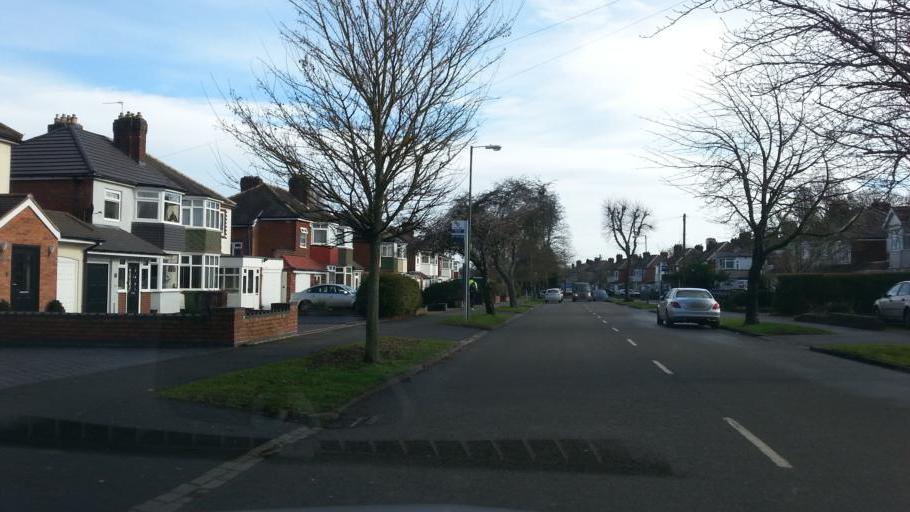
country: GB
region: England
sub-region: City and Borough of Birmingham
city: Acocks Green
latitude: 52.4442
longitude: -1.7934
